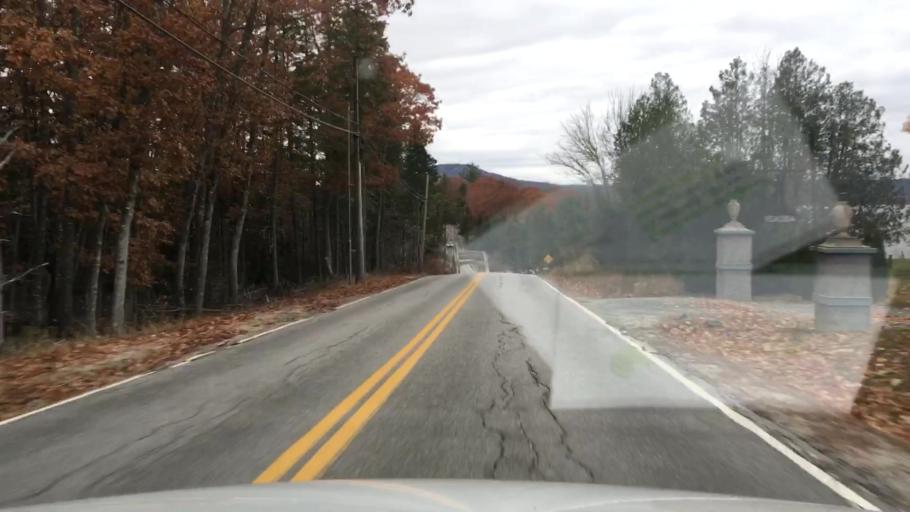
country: US
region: Maine
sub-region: Hancock County
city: Sedgwick
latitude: 44.3720
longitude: -68.5584
